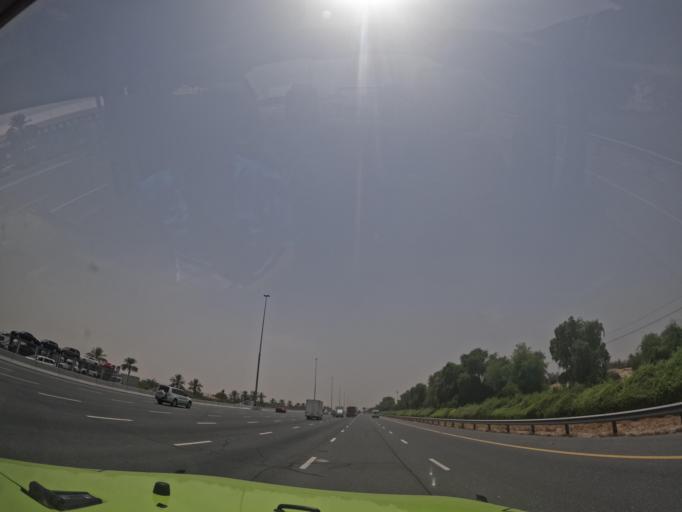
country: AE
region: Dubai
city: Dubai
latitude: 25.0833
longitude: 55.3134
